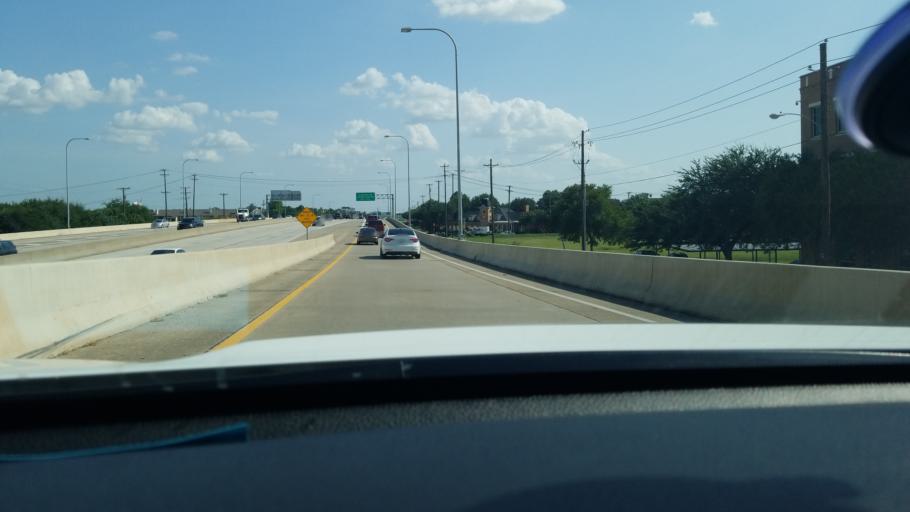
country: US
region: Texas
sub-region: Dallas County
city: Addison
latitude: 33.0093
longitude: -96.8295
